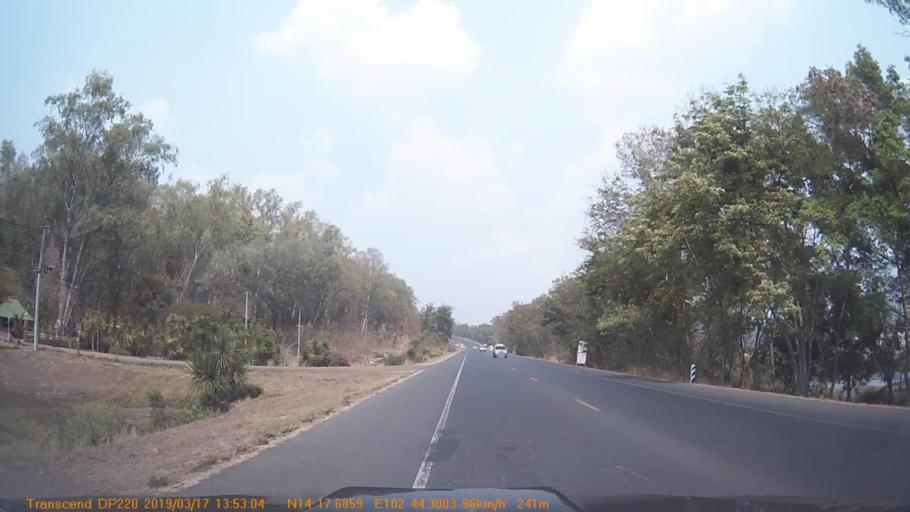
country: TH
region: Buriram
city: Non Din Daeng
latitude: 14.2950
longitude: 102.7387
